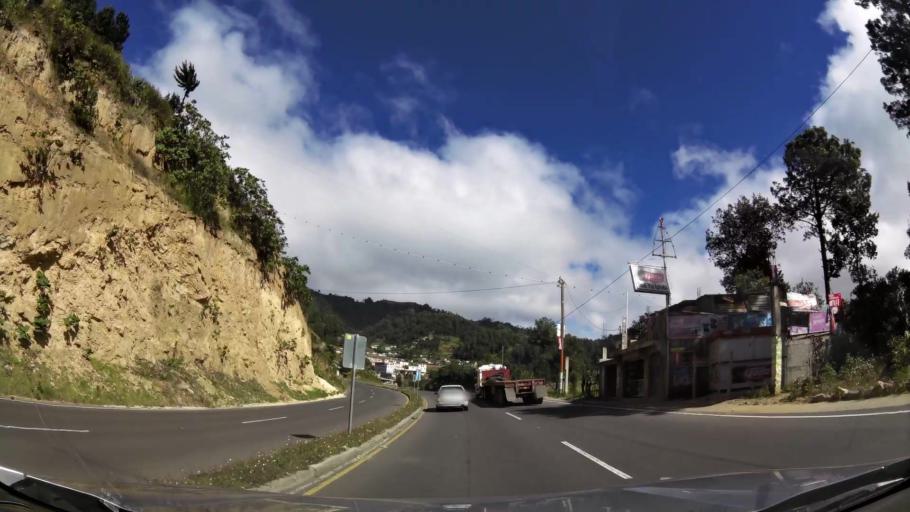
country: GT
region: Solola
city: Concepcion
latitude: 14.8394
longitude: -91.1767
